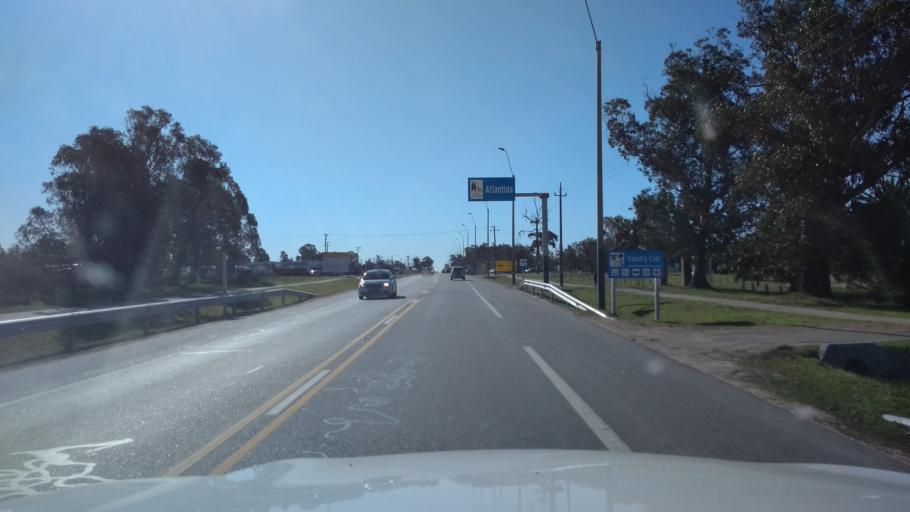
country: UY
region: Canelones
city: Atlantida
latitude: -34.7635
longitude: -55.7649
